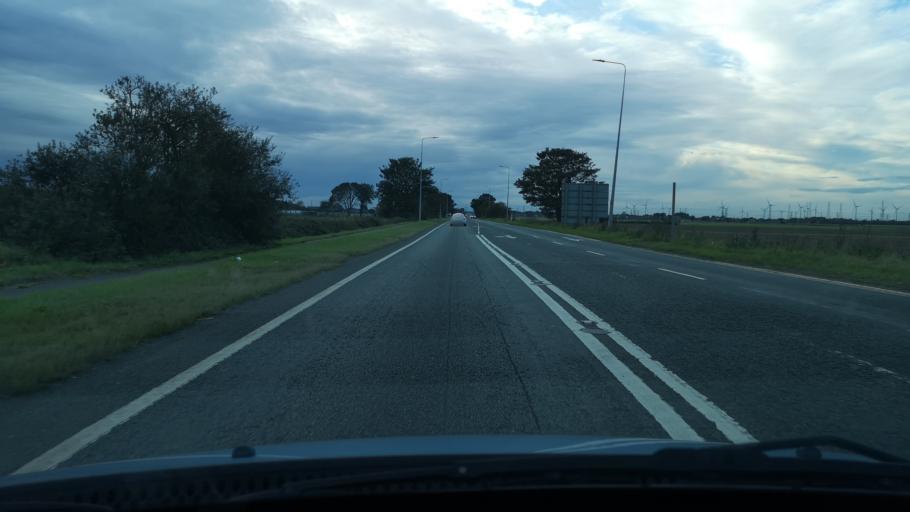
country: GB
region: England
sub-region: North Lincolnshire
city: Gunness
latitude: 53.5896
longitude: -0.7031
